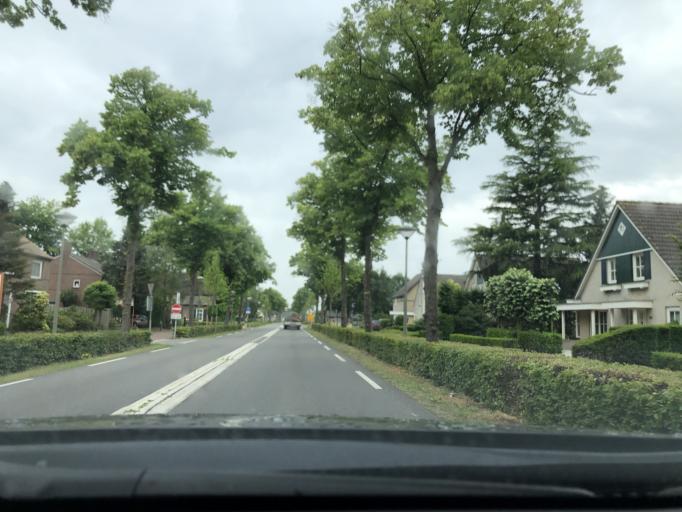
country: NL
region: North Brabant
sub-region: Gemeente Oss
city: Berghem
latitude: 51.7695
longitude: 5.5607
